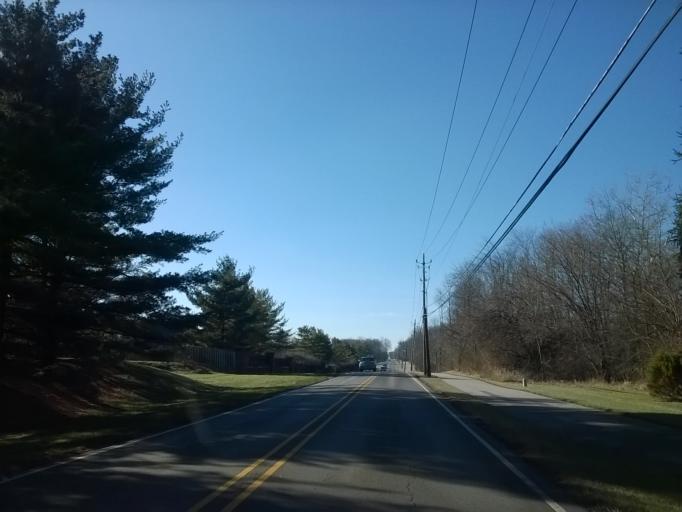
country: US
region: Indiana
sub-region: Marion County
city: Meridian Hills
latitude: 39.9414
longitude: -86.1929
